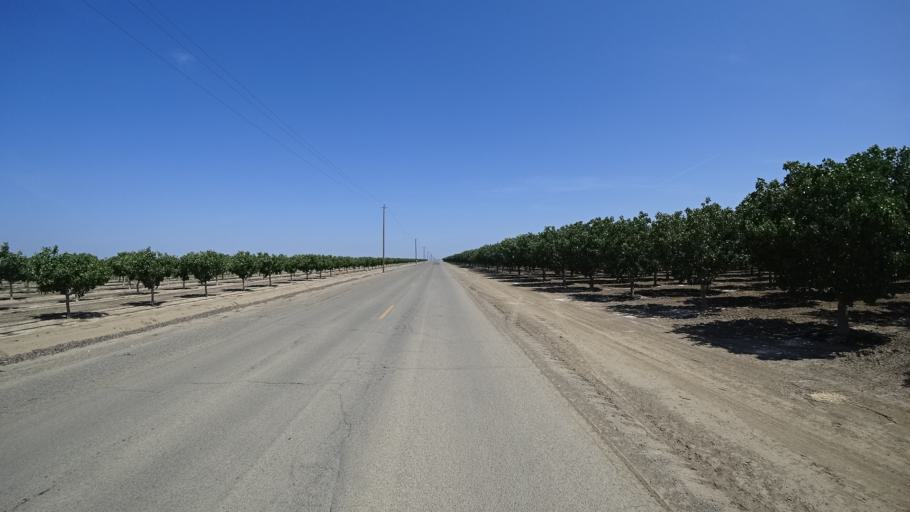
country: US
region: California
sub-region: Kings County
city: Kettleman City
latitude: 36.1027
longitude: -120.0037
